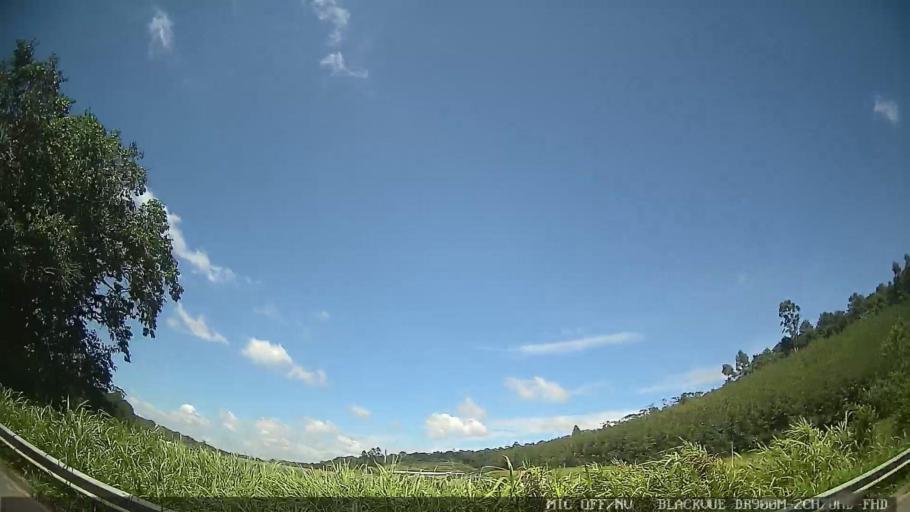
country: BR
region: Sao Paulo
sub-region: Biritiba-Mirim
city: Biritiba Mirim
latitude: -23.5665
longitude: -46.1045
